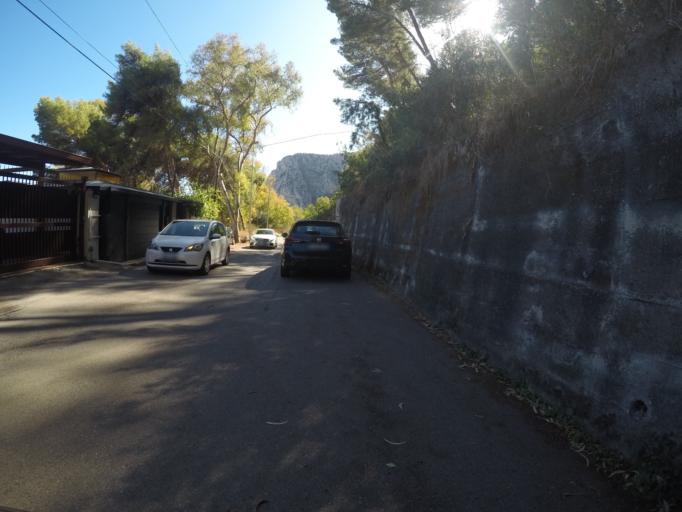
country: IT
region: Sicily
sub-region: Palermo
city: Palermo
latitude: 38.1886
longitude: 13.3416
